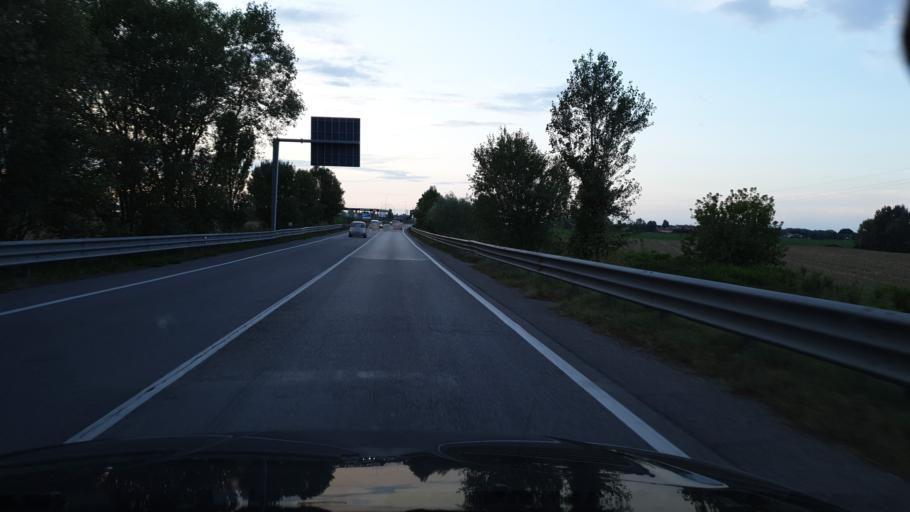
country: IT
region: Emilia-Romagna
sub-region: Provincia di Ravenna
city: Savio
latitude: 44.3070
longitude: 12.2873
